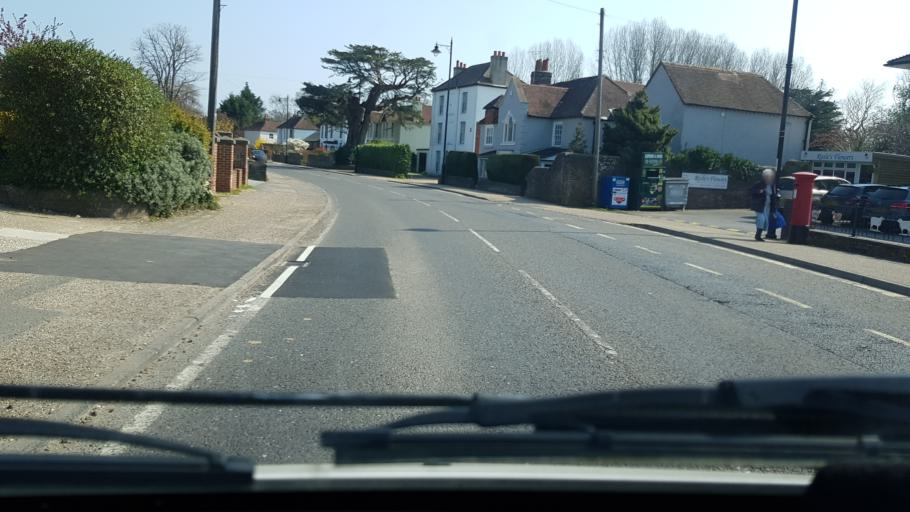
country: GB
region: England
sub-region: West Sussex
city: Chichester
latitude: 50.8355
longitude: -0.8097
